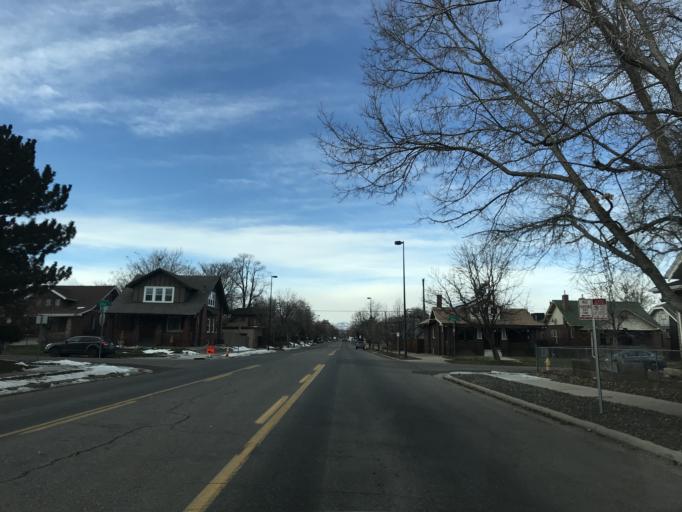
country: US
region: Colorado
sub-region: Denver County
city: Denver
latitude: 39.7645
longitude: -104.9617
